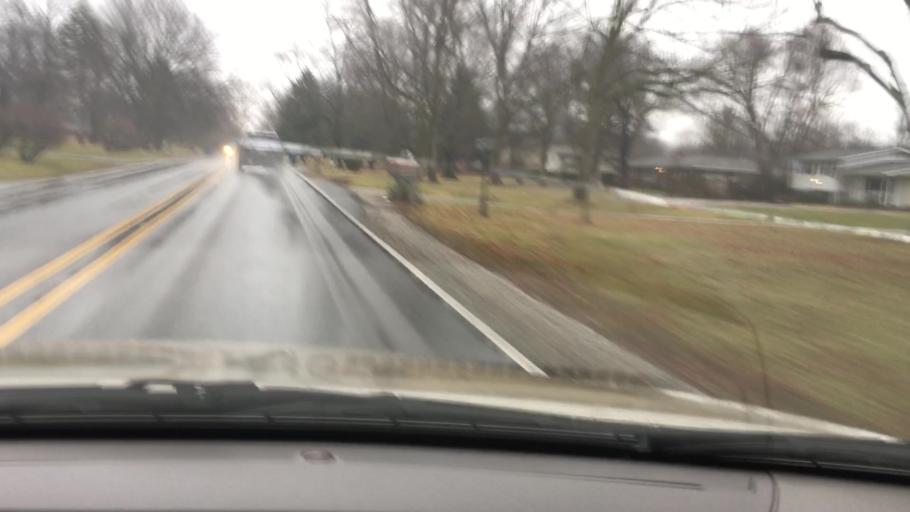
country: US
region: Indiana
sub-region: Marion County
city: Broad Ripple
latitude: 39.8832
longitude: -86.0864
